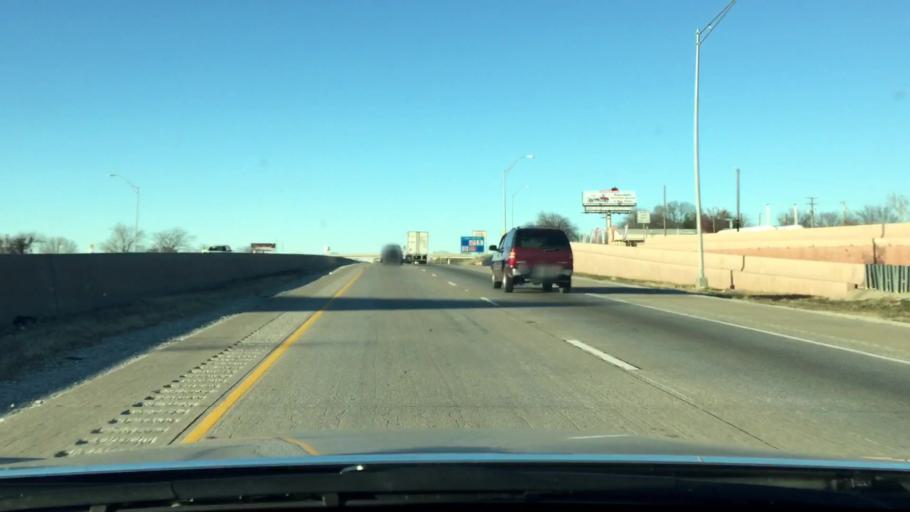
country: US
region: Texas
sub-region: Denton County
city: Sanger
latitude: 33.3467
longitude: -97.1818
